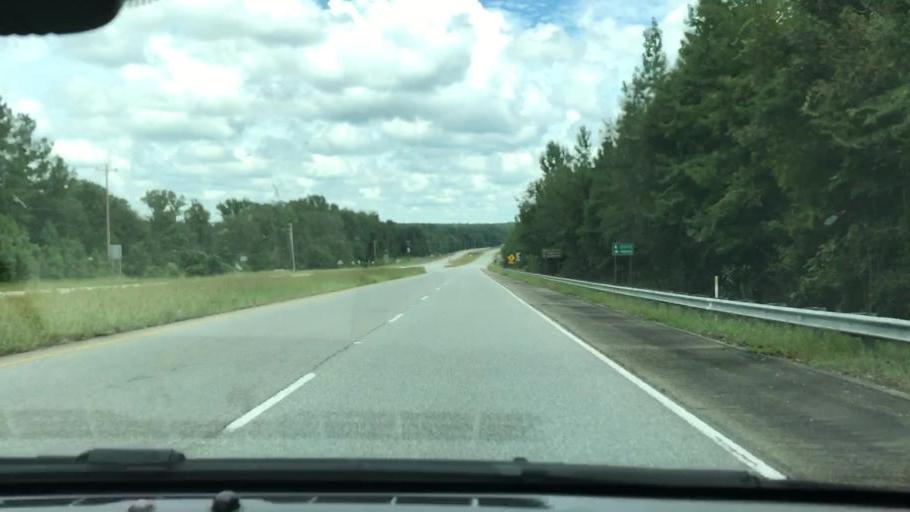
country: US
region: Georgia
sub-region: Stewart County
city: Lumpkin
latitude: 32.1461
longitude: -84.8269
